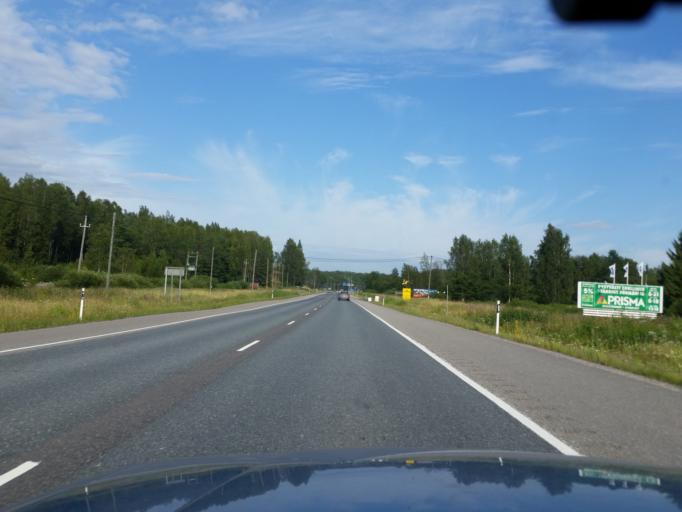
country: FI
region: Uusimaa
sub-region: Helsinki
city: Siuntio
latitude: 60.0936
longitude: 24.2375
